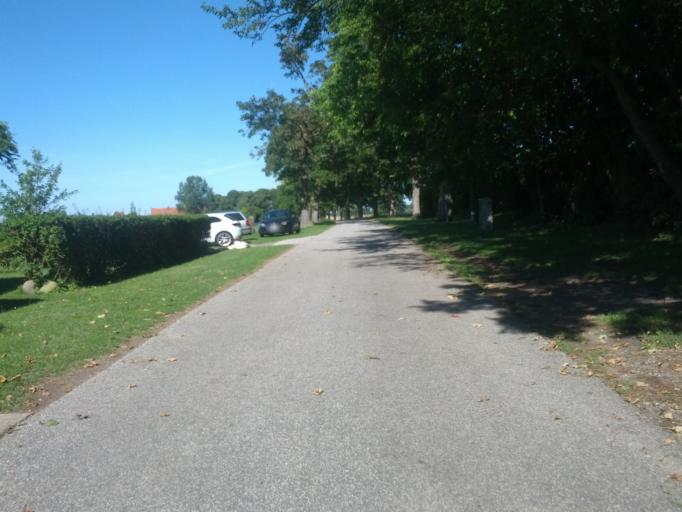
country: DE
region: Mecklenburg-Vorpommern
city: Bastorf
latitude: 54.1065
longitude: 11.6575
